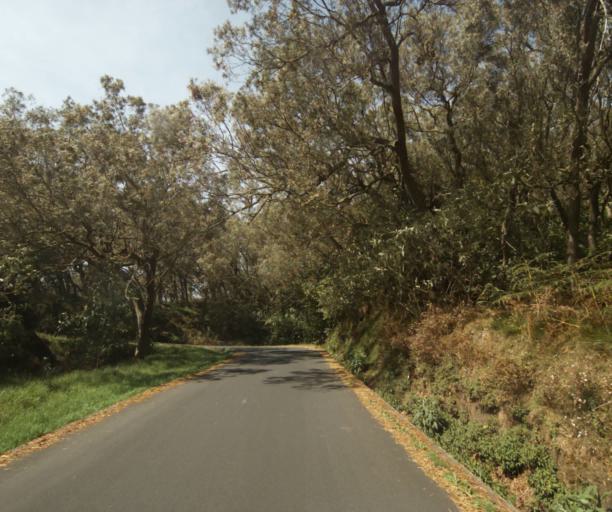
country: RE
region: Reunion
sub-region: Reunion
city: Trois-Bassins
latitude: -21.0591
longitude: 55.3670
